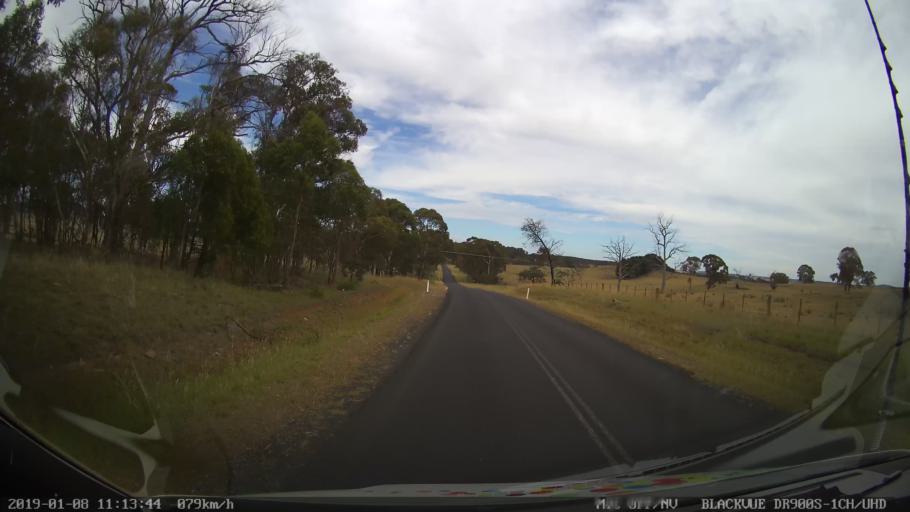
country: AU
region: New South Wales
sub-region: Guyra
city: Guyra
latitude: -30.2290
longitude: 151.5965
